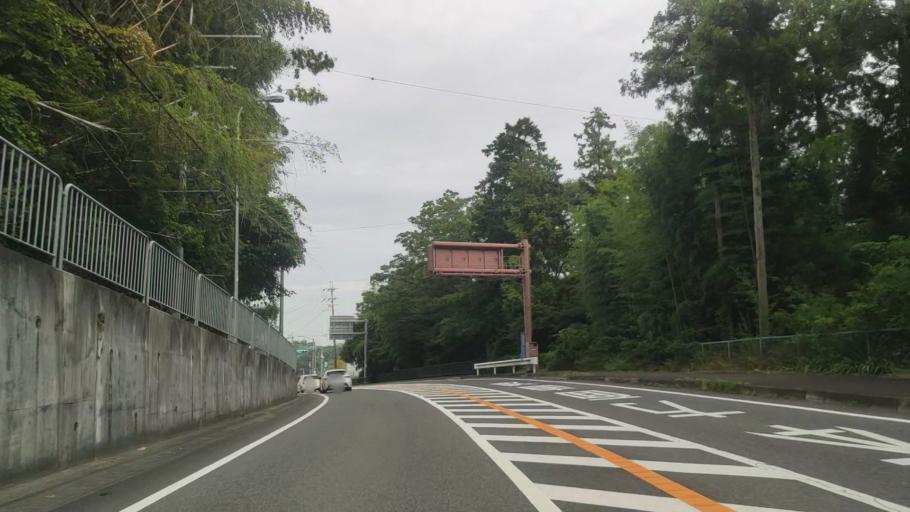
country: JP
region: Osaka
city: Tondabayashicho
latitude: 34.4229
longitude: 135.5779
